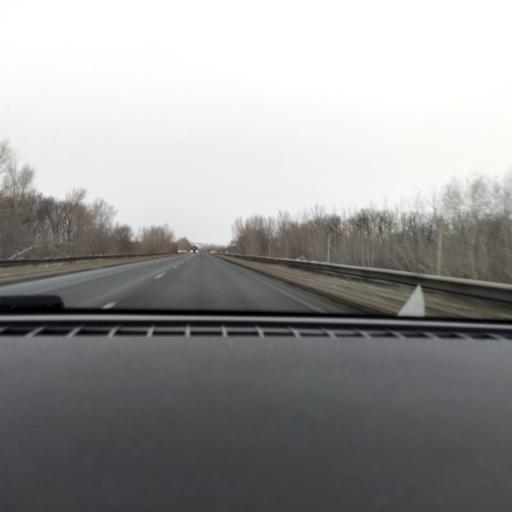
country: RU
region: Samara
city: Kinel'
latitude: 53.2039
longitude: 50.5088
